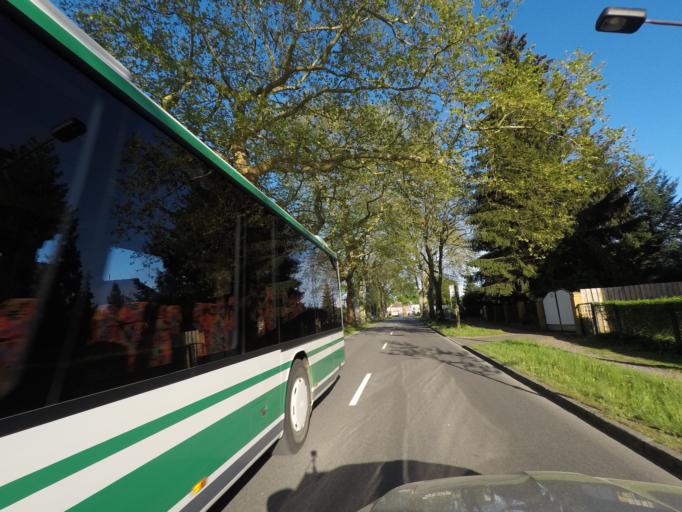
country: DE
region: Brandenburg
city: Eberswalde
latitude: 52.8273
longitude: 13.8429
